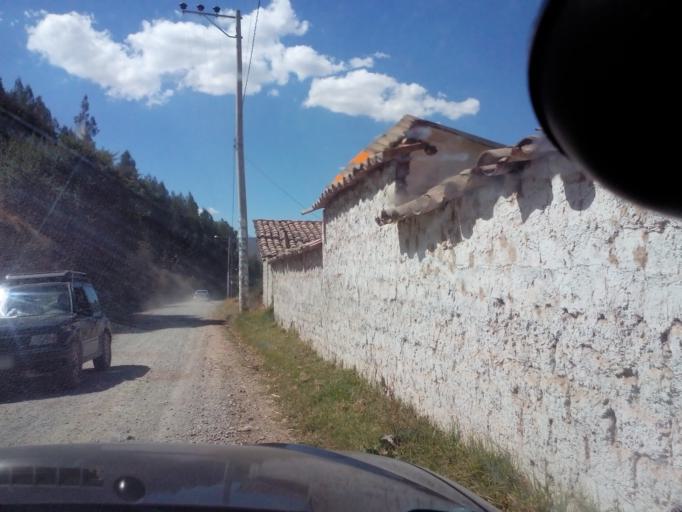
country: PE
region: Cusco
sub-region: Provincia de Anta
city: Huarocondo
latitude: -13.4337
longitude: -72.2242
